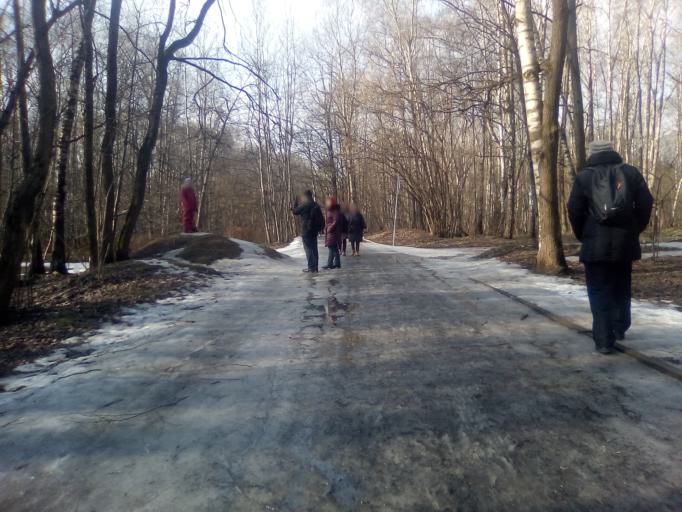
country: RU
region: Moscow
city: Tyoply Stan
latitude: 55.6360
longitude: 37.5069
